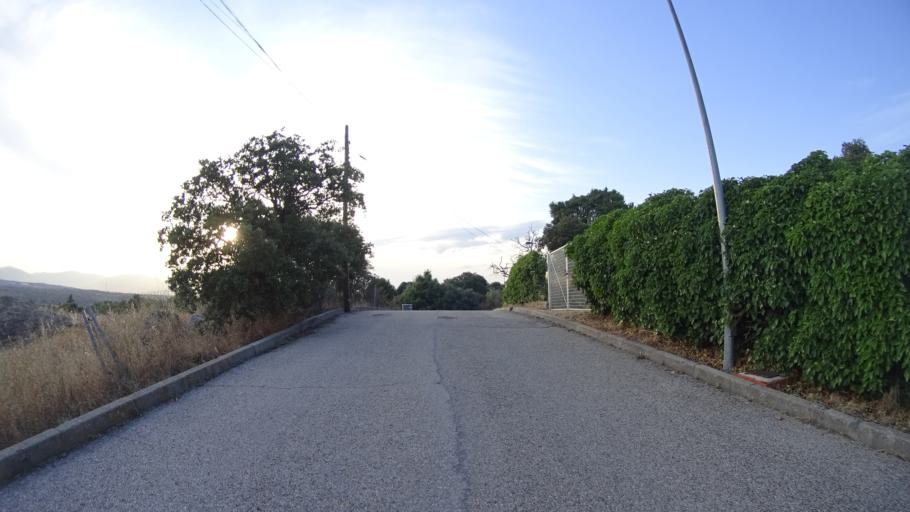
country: ES
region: Madrid
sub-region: Provincia de Madrid
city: Torrelodones
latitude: 40.5881
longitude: -3.9445
